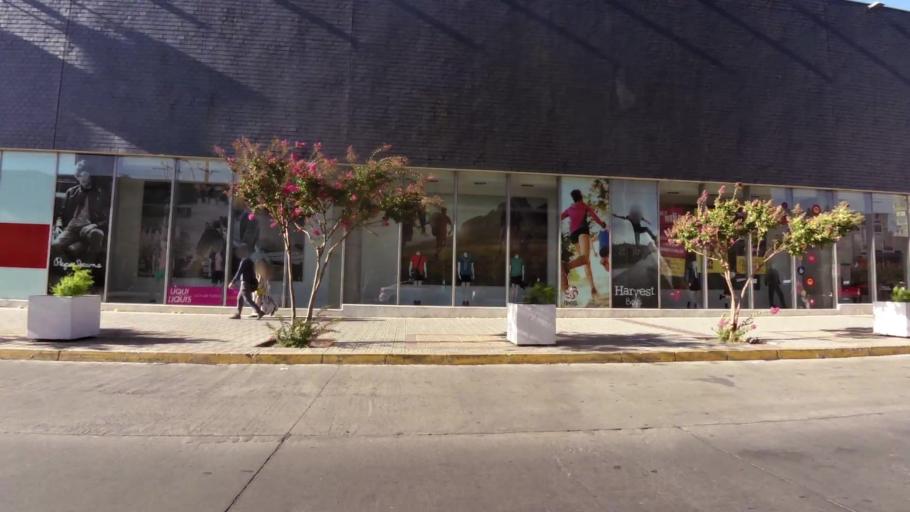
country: CL
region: Maule
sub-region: Provincia de Talca
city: Talca
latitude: -35.4269
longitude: -71.6549
